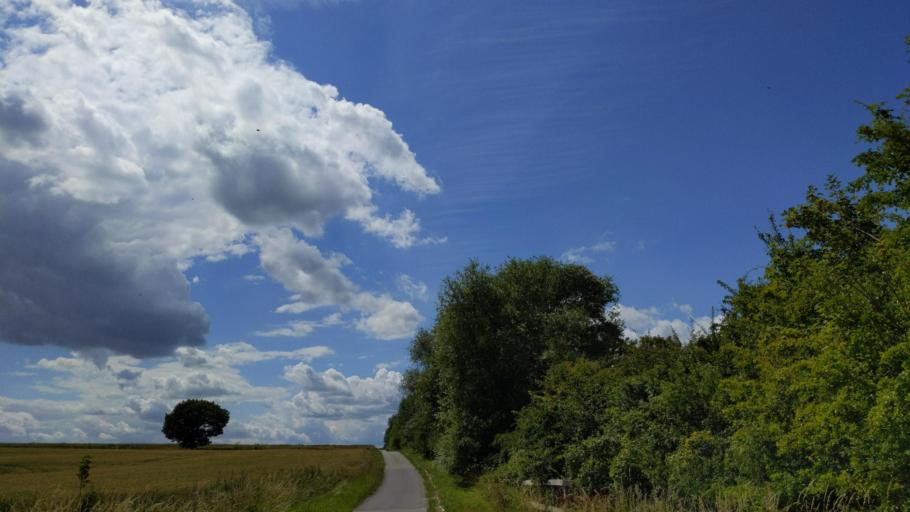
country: DE
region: Mecklenburg-Vorpommern
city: Kalkhorst
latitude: 54.0120
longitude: 11.0868
